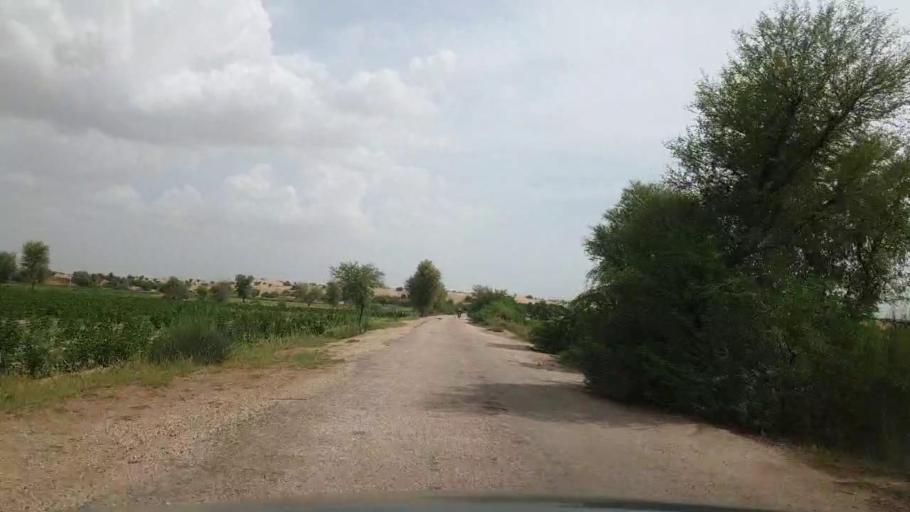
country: PK
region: Sindh
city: Bozdar
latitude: 27.0808
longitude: 69.0136
